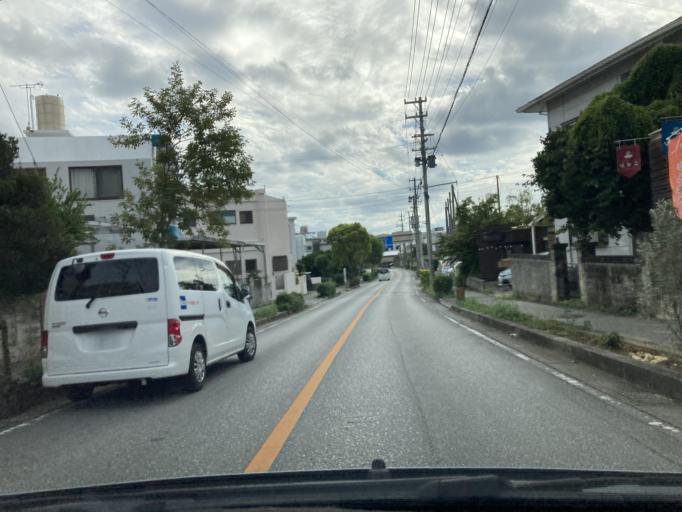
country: JP
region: Okinawa
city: Itoman
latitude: 26.1285
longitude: 127.6782
